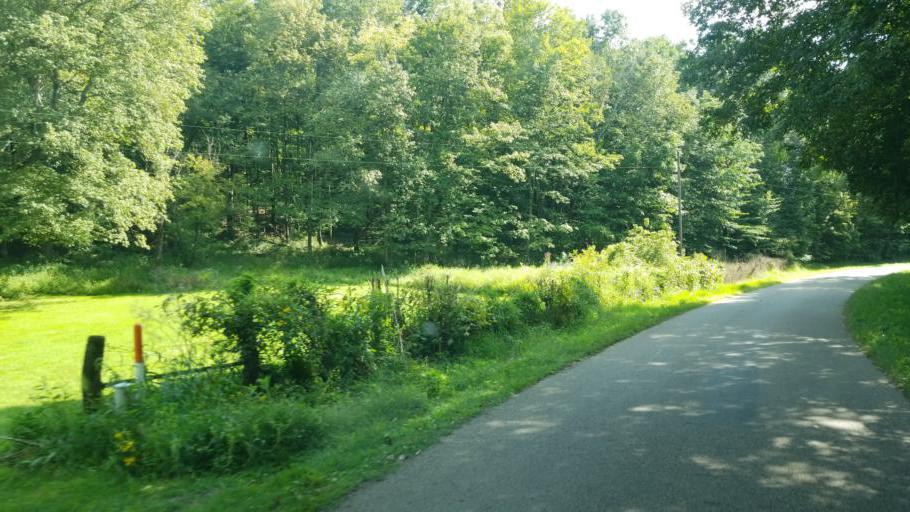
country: US
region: Ohio
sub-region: Knox County
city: Gambier
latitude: 40.3951
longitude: -82.3299
